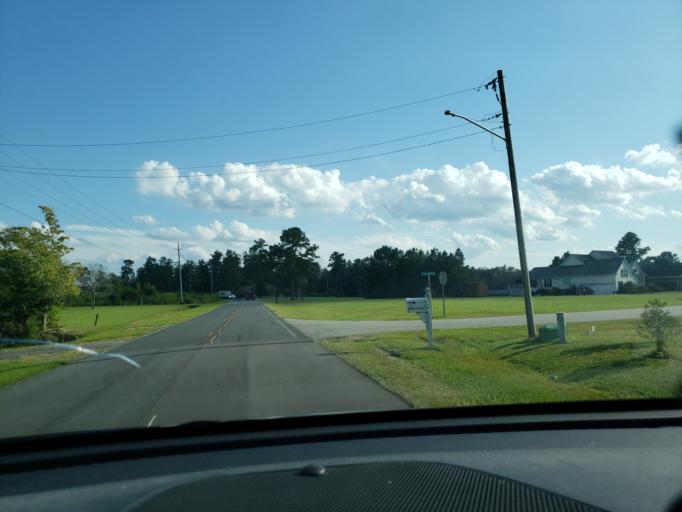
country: US
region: North Carolina
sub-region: Columbus County
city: Tabor City
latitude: 34.1646
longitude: -78.8517
